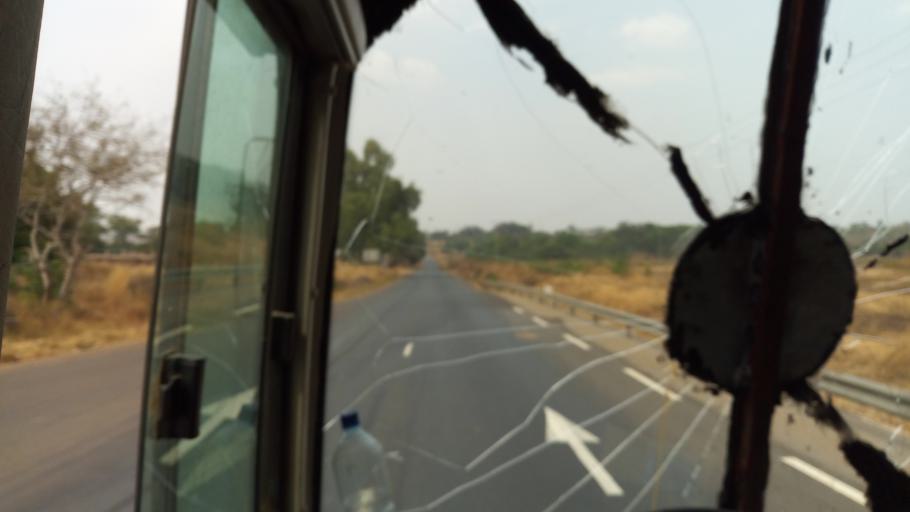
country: TG
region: Kara
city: Bafilo
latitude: 9.2817
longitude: 1.2368
